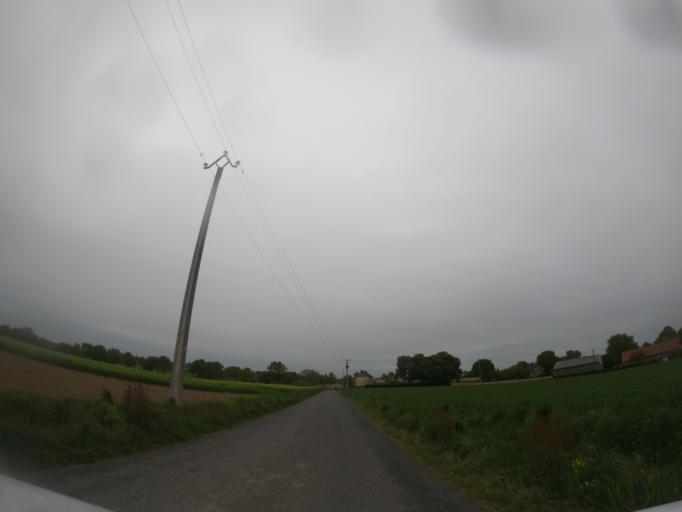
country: FR
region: Brittany
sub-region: Departement d'Ille-et-Vilaine
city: Argentre-du-Plessis
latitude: 47.9637
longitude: -1.1223
